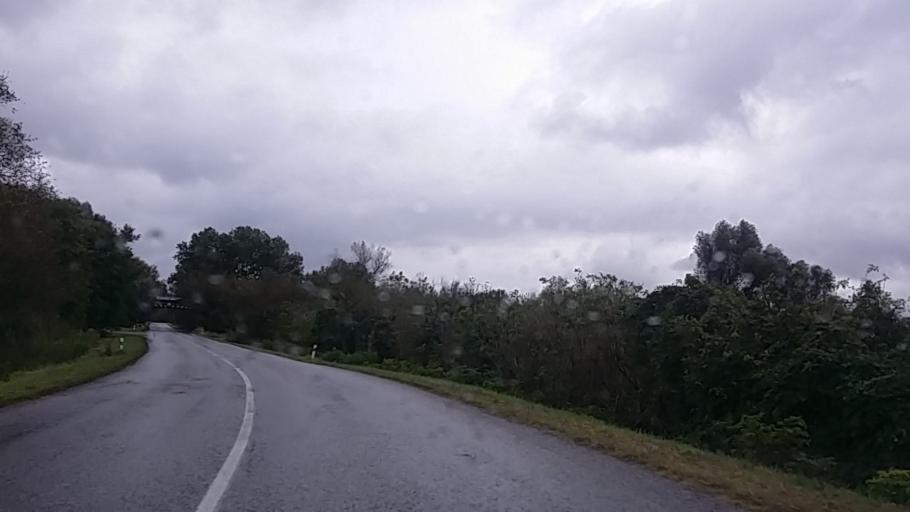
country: SK
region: Nitriansky
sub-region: Okres Nove Zamky
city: Sturovo
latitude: 47.8170
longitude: 18.7183
